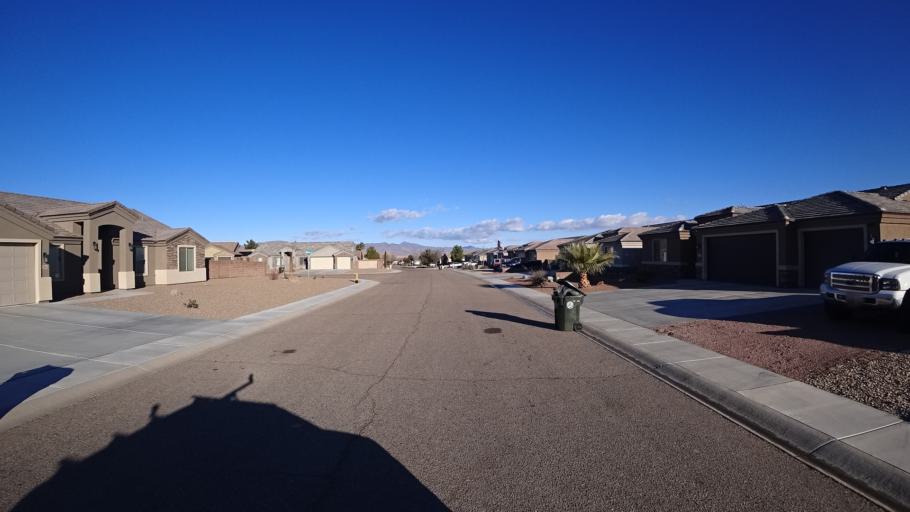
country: US
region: Arizona
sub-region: Mohave County
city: New Kingman-Butler
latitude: 35.2202
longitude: -113.9703
